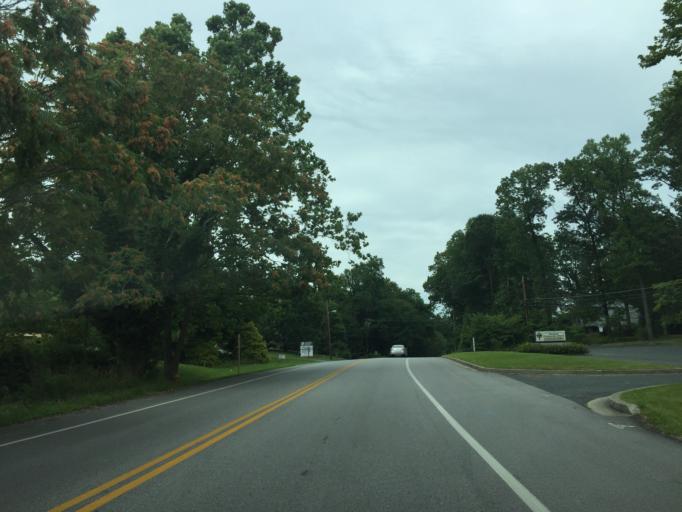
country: US
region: Maryland
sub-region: Baltimore County
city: Hampton
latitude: 39.4127
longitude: -76.5771
